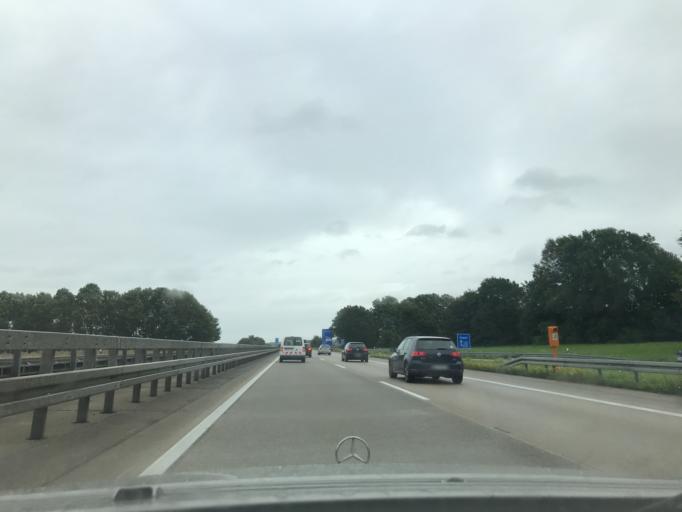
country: DE
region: North Rhine-Westphalia
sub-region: Regierungsbezirk Detmold
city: Buren
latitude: 51.5969
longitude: 8.5705
